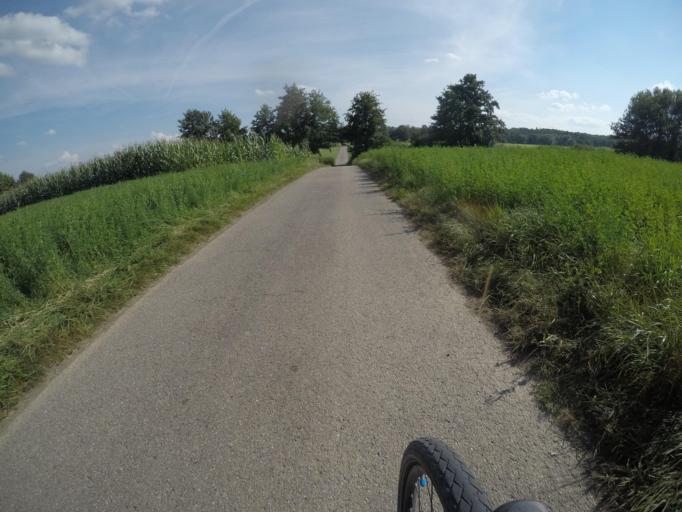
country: DE
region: Baden-Wuerttemberg
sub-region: Karlsruhe Region
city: Olbronn-Durrn
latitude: 48.9654
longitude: 8.7525
